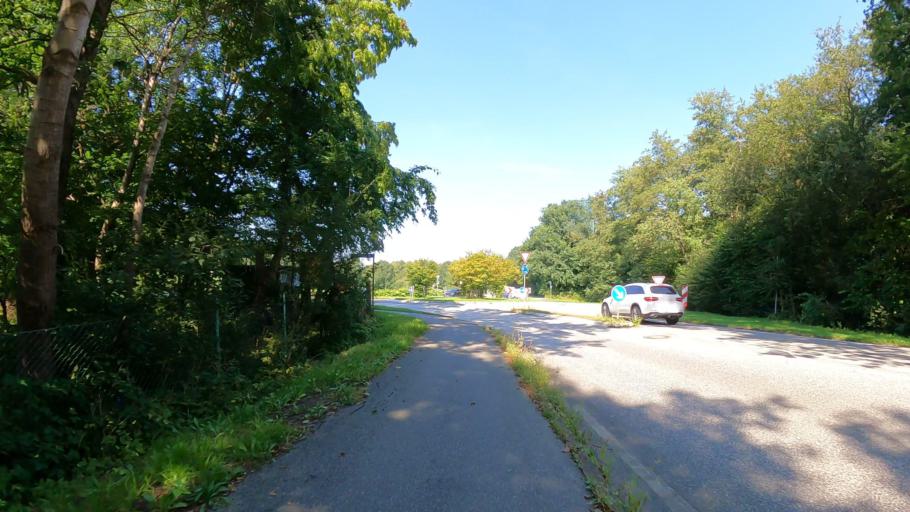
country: DE
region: Schleswig-Holstein
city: Bad Bramstedt
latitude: 53.9006
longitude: 9.8834
